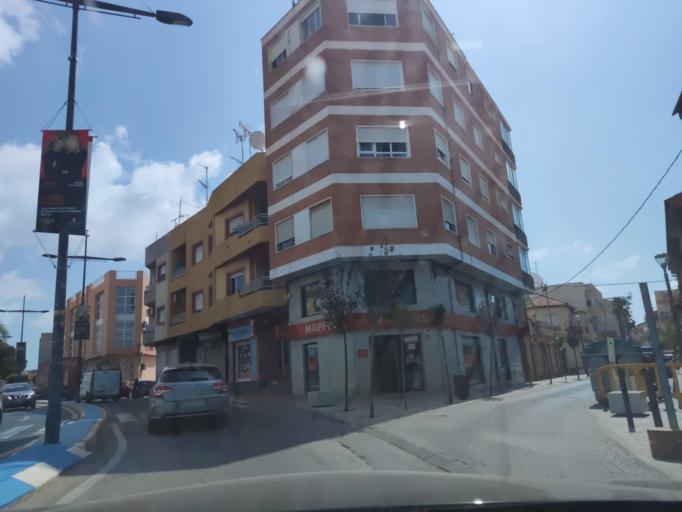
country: ES
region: Murcia
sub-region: Murcia
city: San Javier
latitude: 37.8054
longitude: -0.8376
